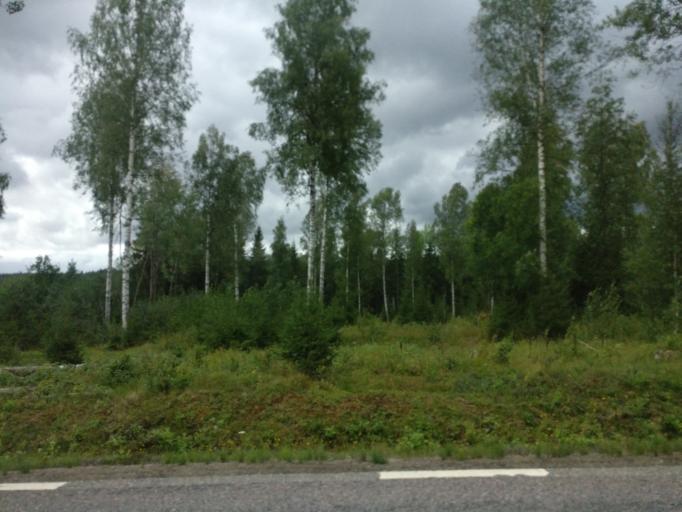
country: SE
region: Vaermland
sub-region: Torsby Kommun
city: Torsby
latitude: 60.7684
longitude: 12.7577
